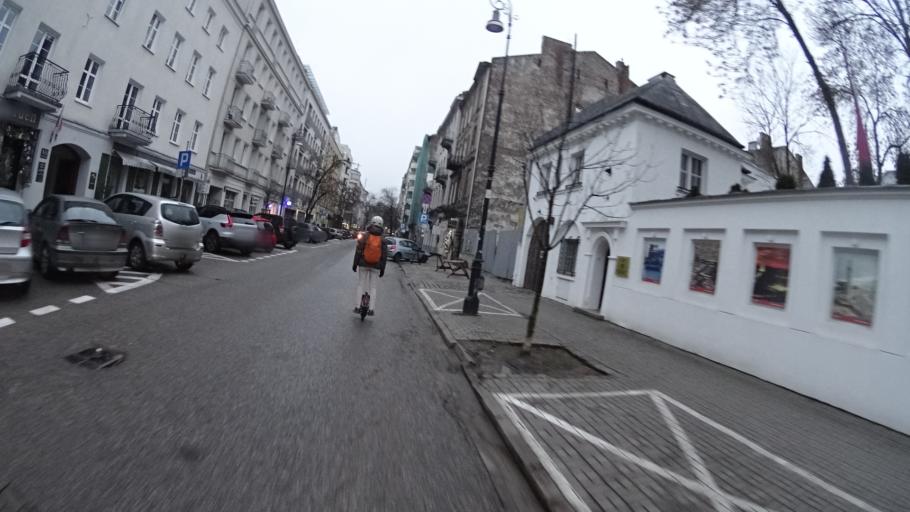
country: PL
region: Masovian Voivodeship
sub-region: Warszawa
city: Warsaw
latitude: 52.2245
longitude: 21.0076
